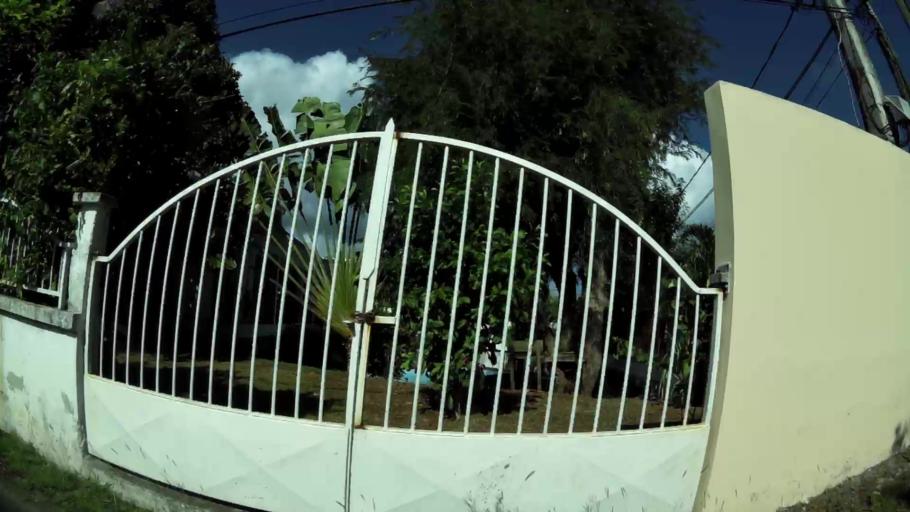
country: GP
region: Guadeloupe
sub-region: Guadeloupe
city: Sainte-Anne
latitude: 16.2339
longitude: -61.3759
